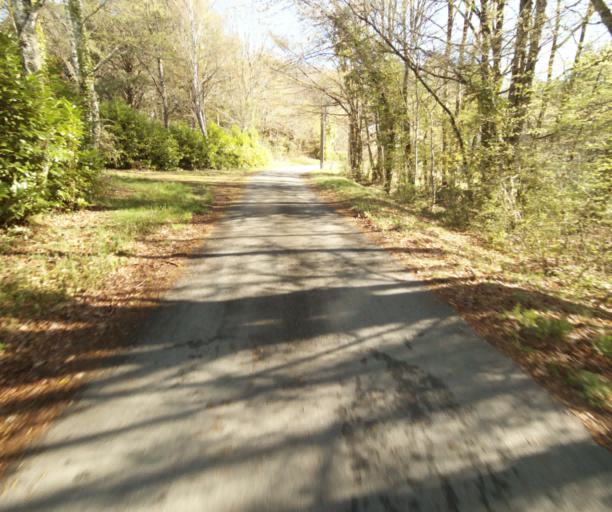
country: FR
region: Limousin
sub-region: Departement de la Correze
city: Laguenne
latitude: 45.2585
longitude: 1.8545
